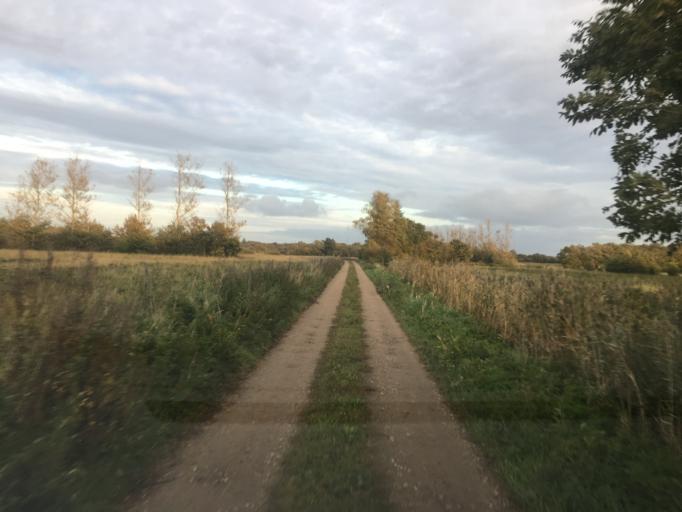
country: DK
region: South Denmark
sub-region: Tonder Kommune
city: Tonder
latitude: 54.9663
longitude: 8.8339
